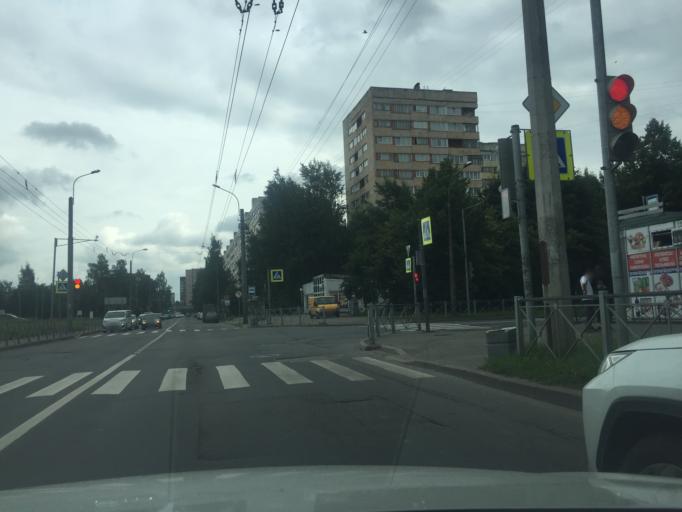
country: RU
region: Leningrad
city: Bugry
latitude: 60.0533
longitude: 30.3715
